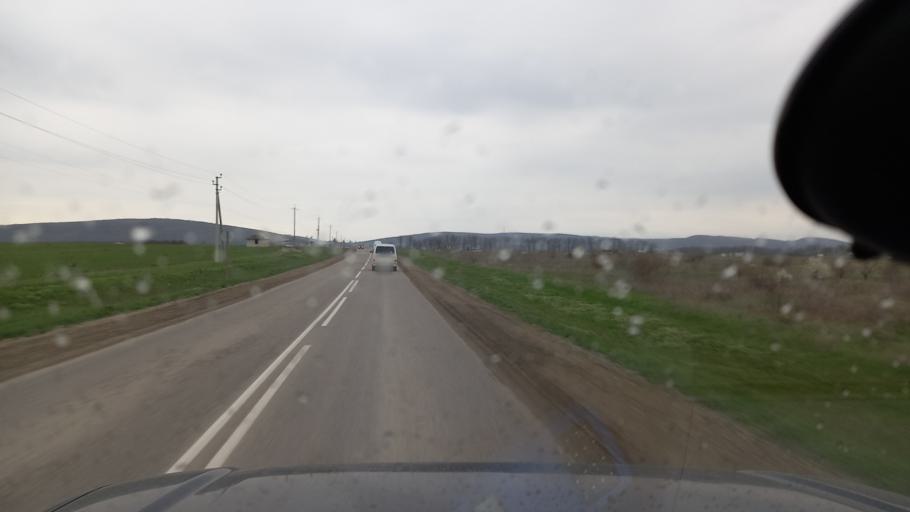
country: RU
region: Krasnodarskiy
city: Anapskaya
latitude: 44.8836
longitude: 37.4520
